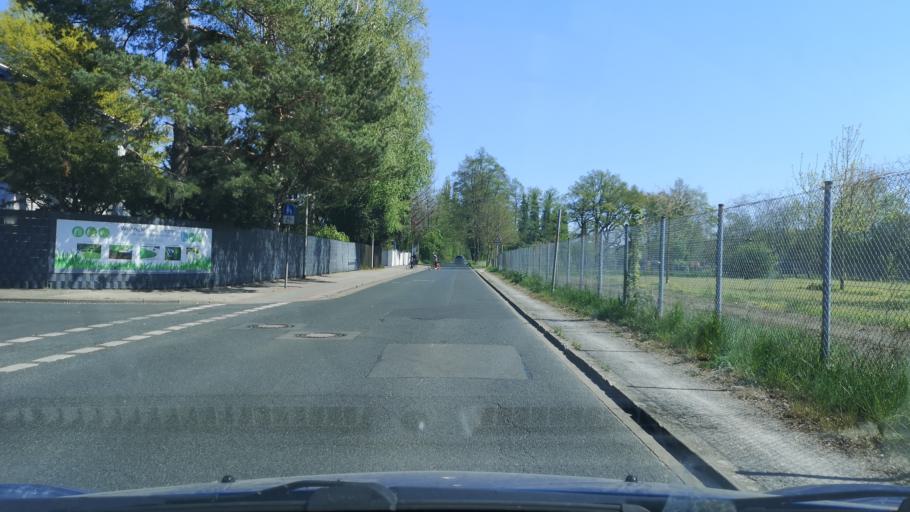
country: DE
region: Lower Saxony
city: Isernhagen Farster Bauerschaft
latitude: 52.4314
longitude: 9.8084
